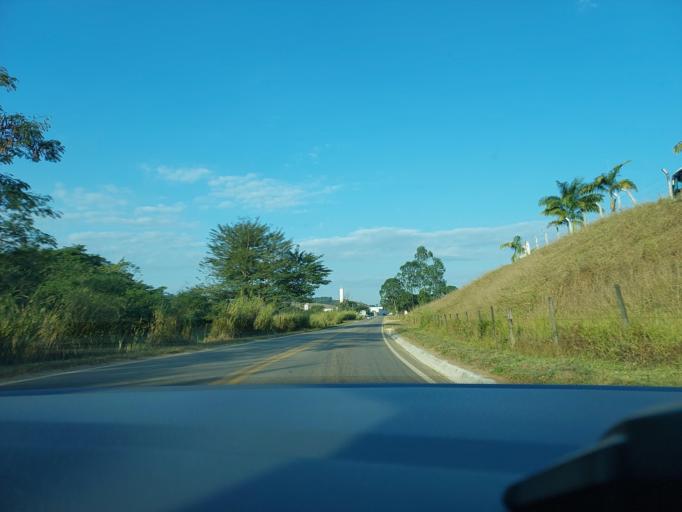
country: BR
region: Minas Gerais
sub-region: Muriae
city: Muriae
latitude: -21.1193
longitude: -42.4094
